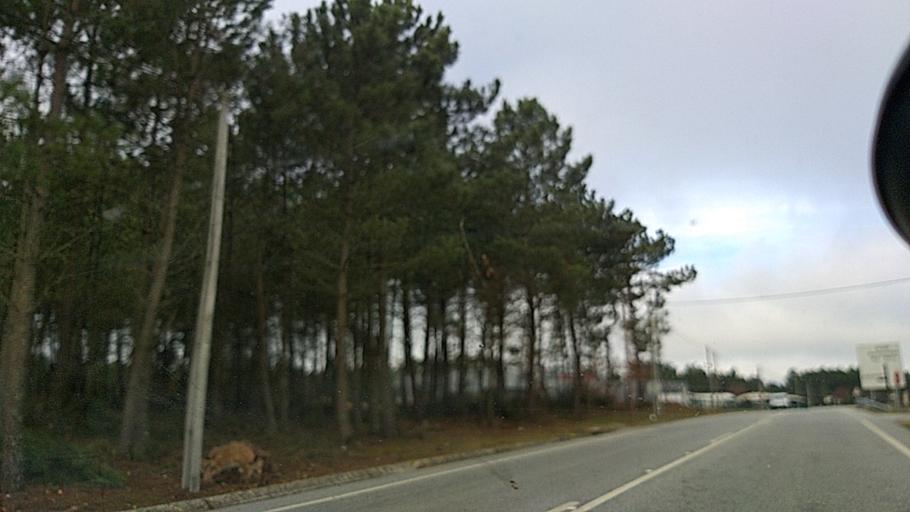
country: PT
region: Guarda
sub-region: Aguiar da Beira
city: Aguiar da Beira
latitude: 40.7946
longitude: -7.5169
